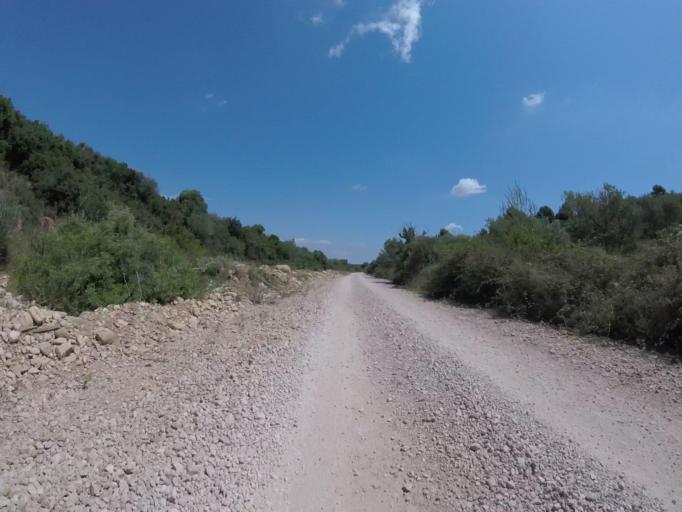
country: ES
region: Valencia
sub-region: Provincia de Castello
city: Torreblanca
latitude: 40.2290
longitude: 0.1581
